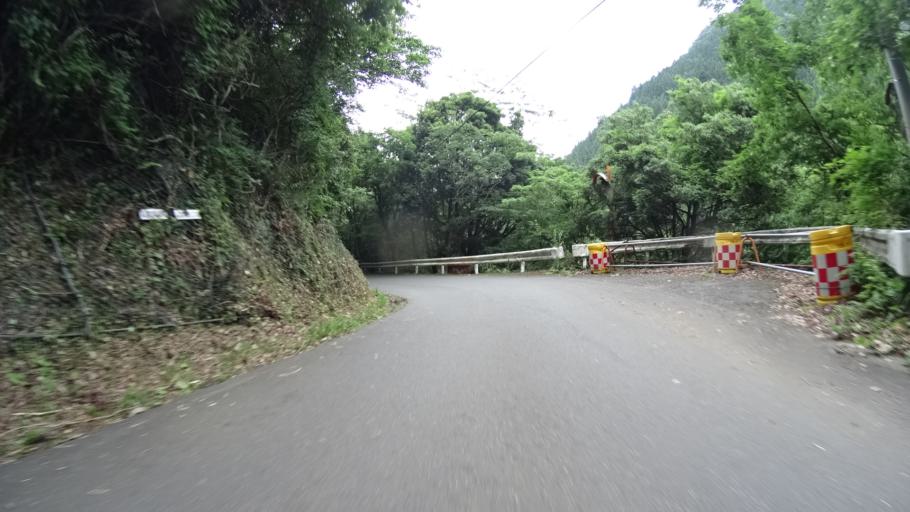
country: JP
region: Kanagawa
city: Hadano
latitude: 35.4907
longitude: 139.2198
